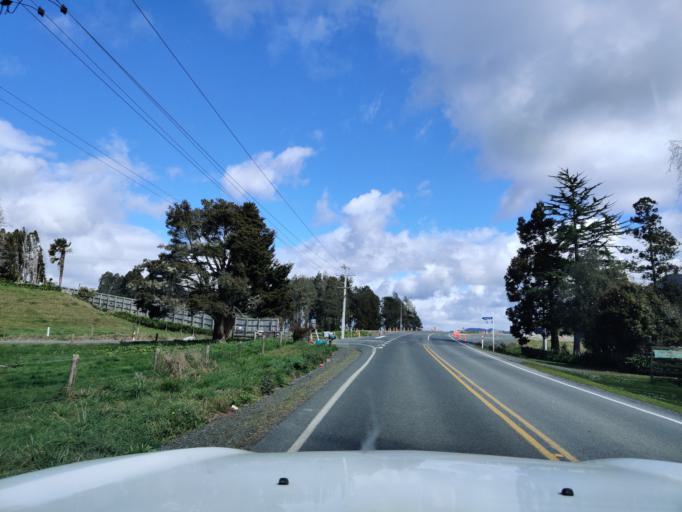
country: NZ
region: Waikato
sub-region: Waikato District
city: Ngaruawahia
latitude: -37.5942
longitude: 175.2076
